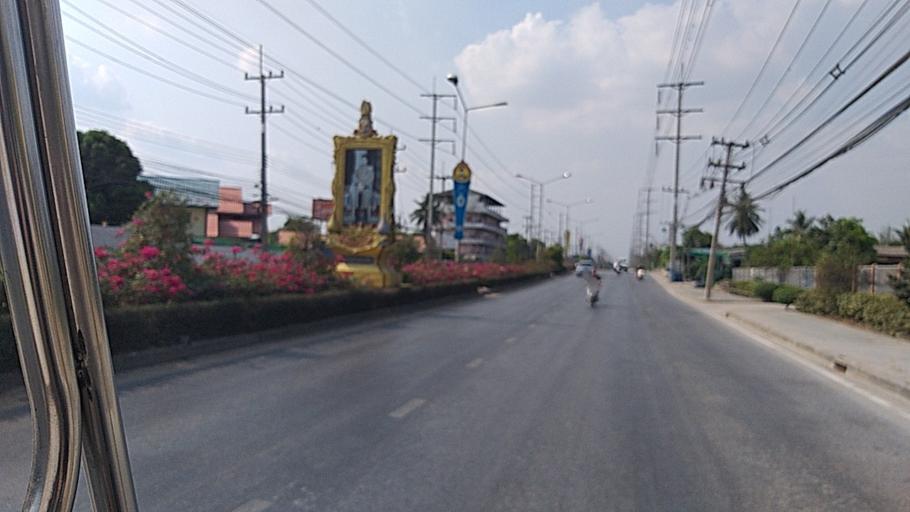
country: TH
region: Pathum Thani
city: Sam Khok
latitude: 14.0581
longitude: 100.5243
